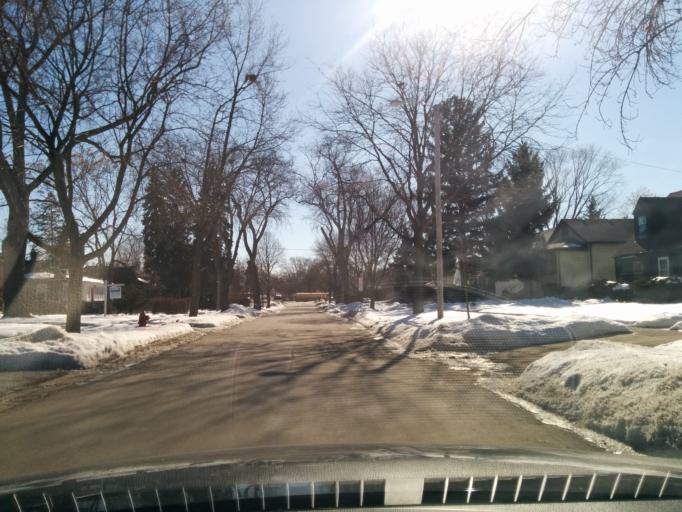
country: US
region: Illinois
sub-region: DuPage County
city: Villa Park
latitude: 41.8913
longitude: -87.9872
